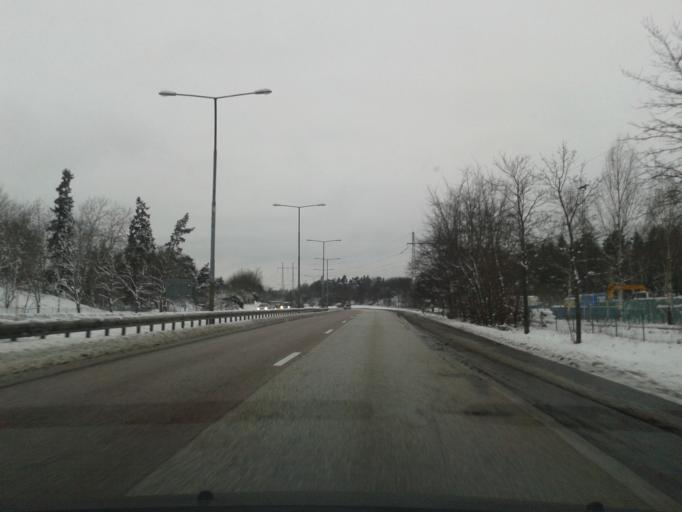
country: SE
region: Stockholm
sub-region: Stockholms Kommun
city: Arsta
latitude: 59.2638
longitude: 18.0636
